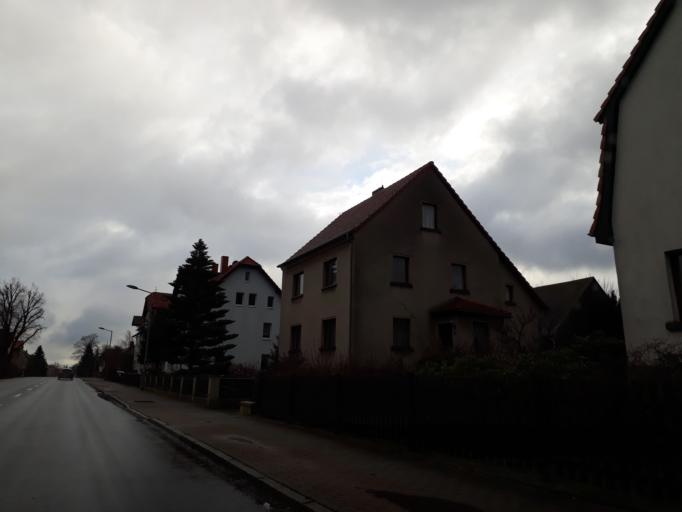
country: DE
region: Saxony
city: Herrnhut
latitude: 51.0242
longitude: 14.7308
